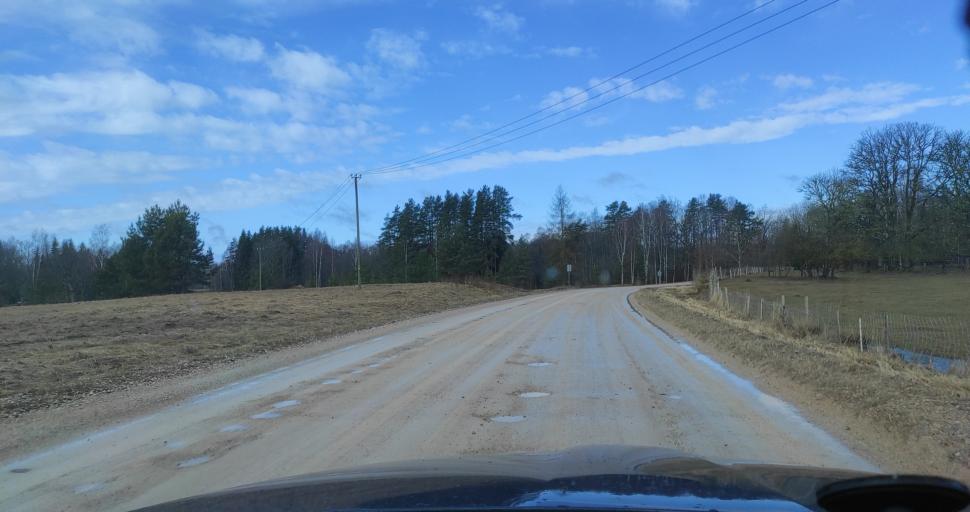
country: LV
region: Tukuma Rajons
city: Tukums
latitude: 57.1091
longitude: 23.0315
